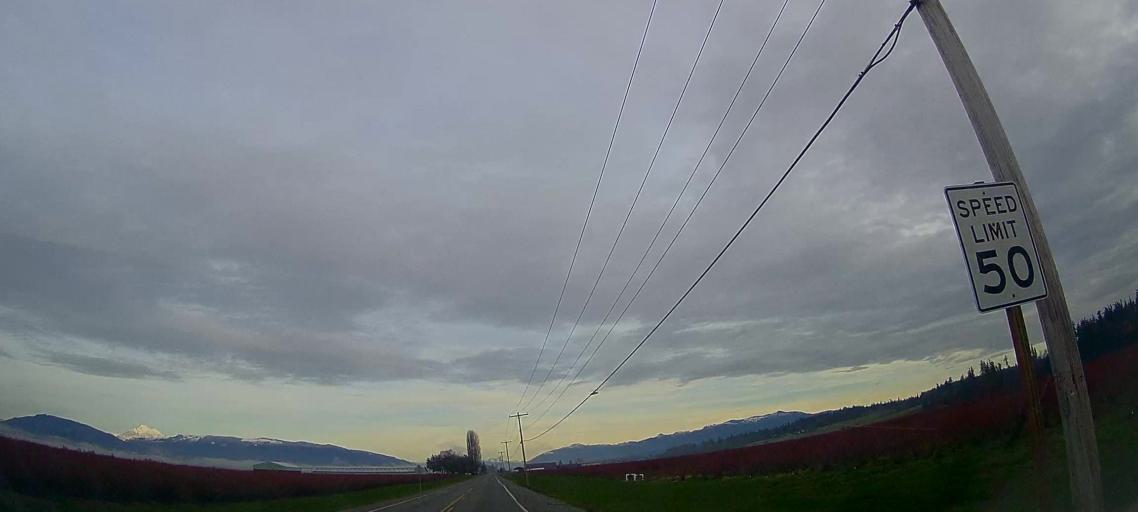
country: US
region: Washington
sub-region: Skagit County
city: Anacortes
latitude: 48.5191
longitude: -122.4709
